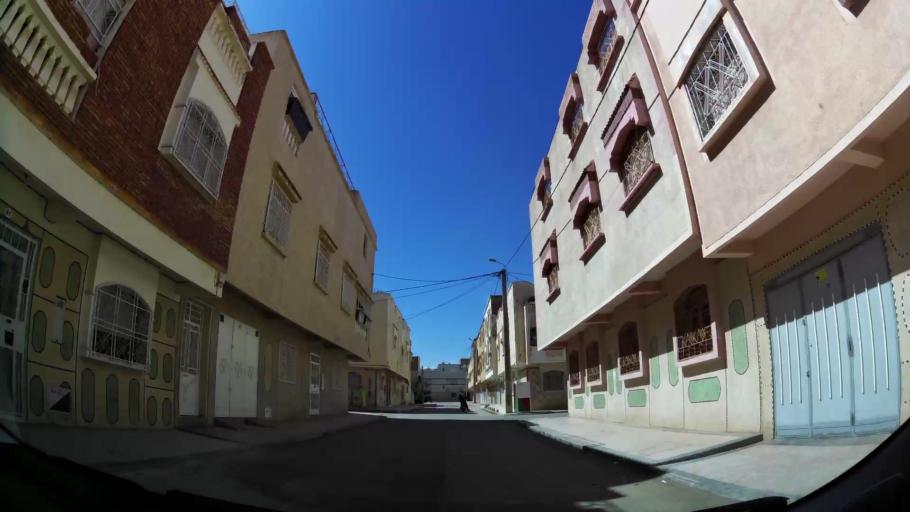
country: MA
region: Oriental
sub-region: Oujda-Angad
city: Oujda
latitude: 34.6630
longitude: -1.8921
